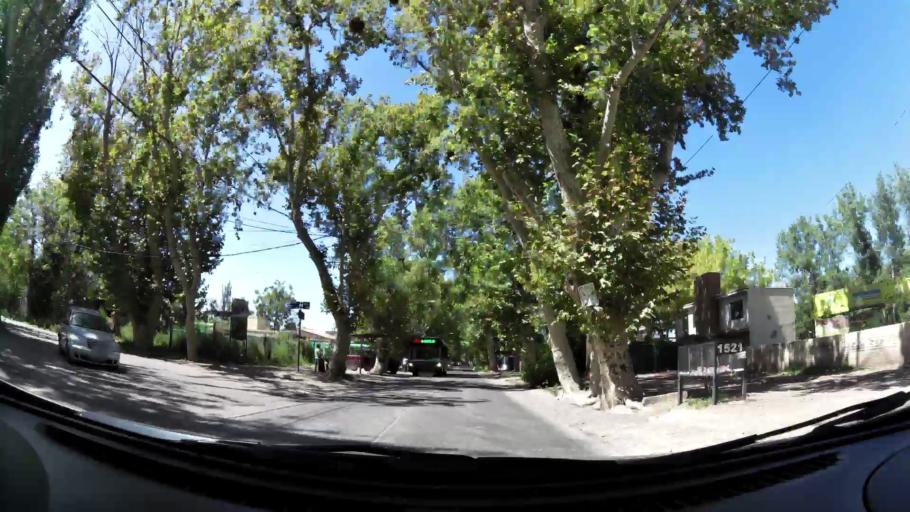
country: AR
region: Mendoza
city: Las Heras
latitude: -32.8697
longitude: -68.8006
